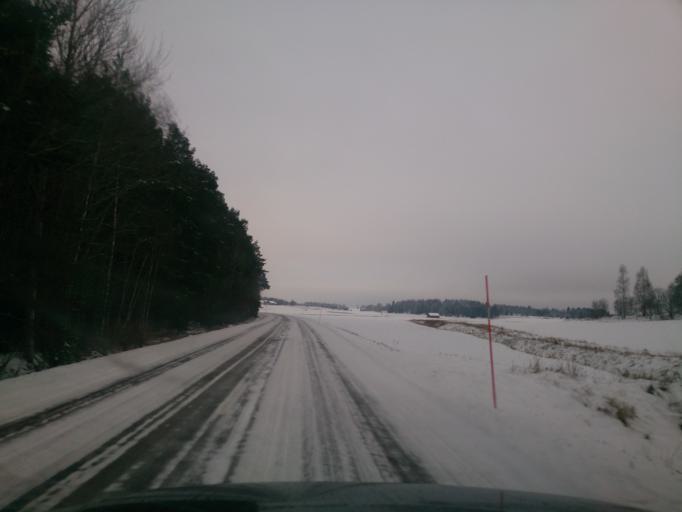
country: SE
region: OEstergoetland
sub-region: Linkopings Kommun
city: Linghem
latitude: 58.4377
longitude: 15.8926
